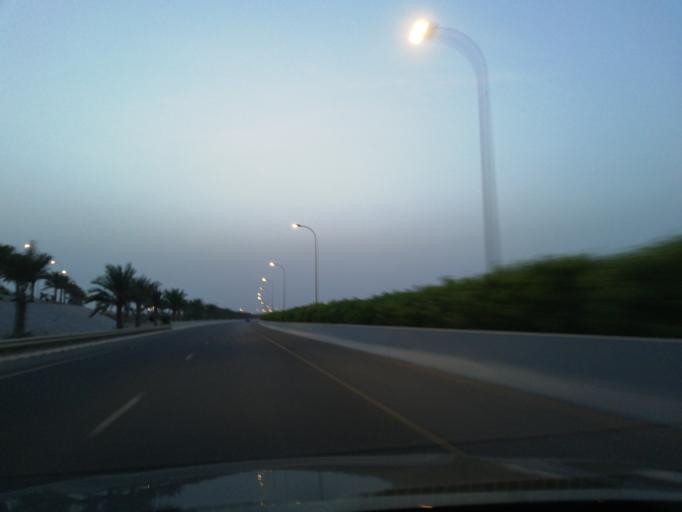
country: OM
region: Muhafazat Masqat
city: Bawshar
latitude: 23.5974
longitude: 58.3332
